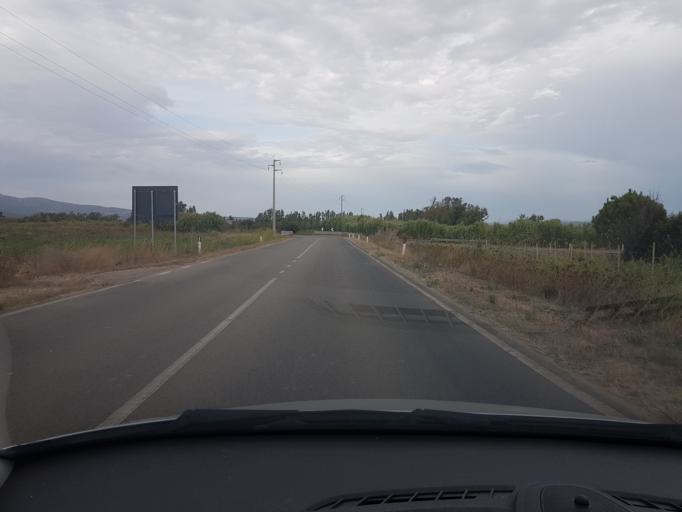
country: IT
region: Sardinia
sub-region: Provincia di Oristano
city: Riola Sardo
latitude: 40.0042
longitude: 8.5366
